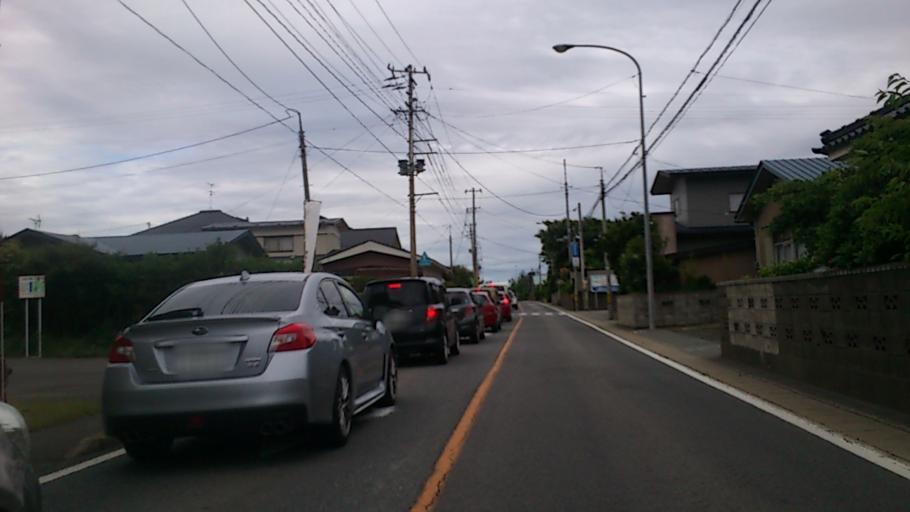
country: JP
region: Akita
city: Akita Shi
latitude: 39.6263
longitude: 140.0648
